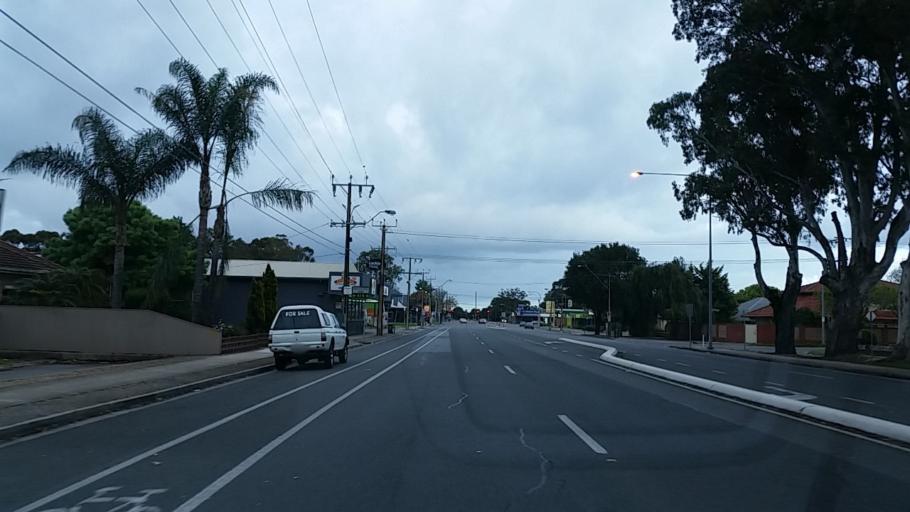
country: AU
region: South Australia
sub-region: Charles Sturt
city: Seaton
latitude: -34.9264
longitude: 138.5205
